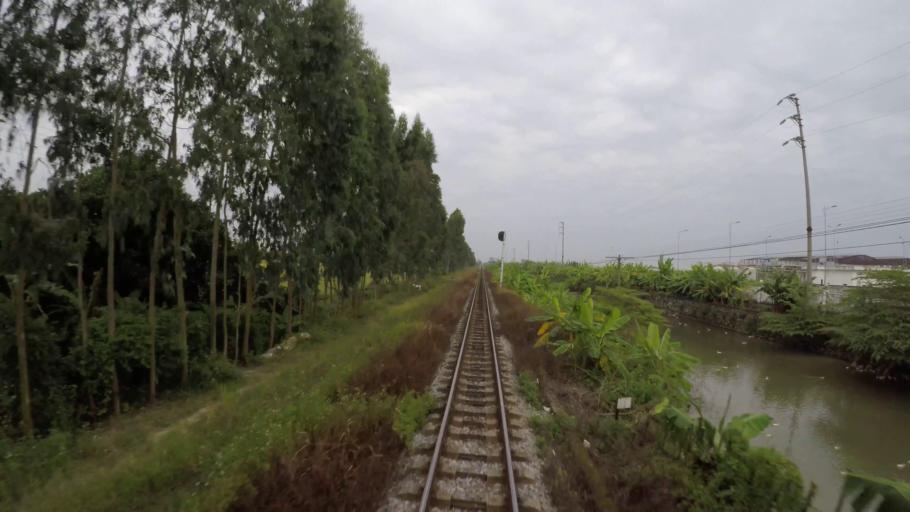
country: VN
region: Hai Duong
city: Lai Cach
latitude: 20.9473
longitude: 106.2600
